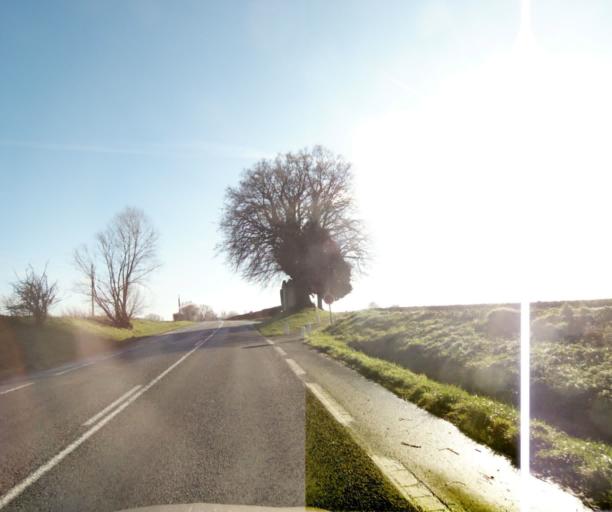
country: FR
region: Nord-Pas-de-Calais
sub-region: Departement du Nord
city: Preseau
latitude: 50.3192
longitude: 3.5671
